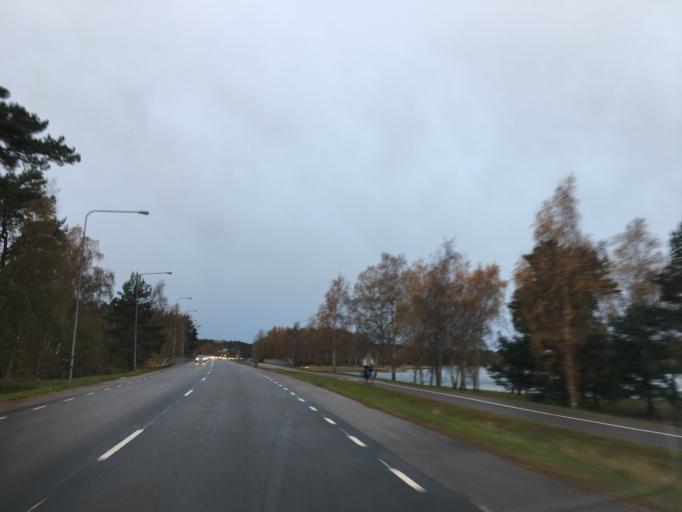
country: SE
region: Kalmar
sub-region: Kalmar Kommun
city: Kalmar
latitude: 56.6754
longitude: 16.3646
